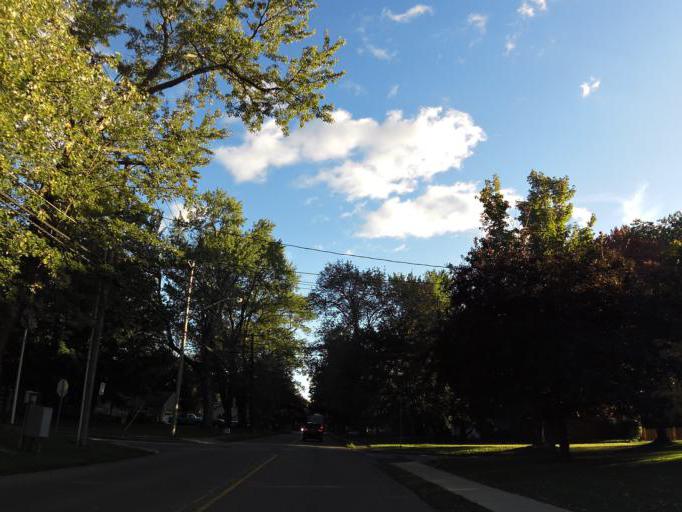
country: US
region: New York
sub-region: Erie County
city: East Aurora
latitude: 42.7736
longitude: -78.6210
